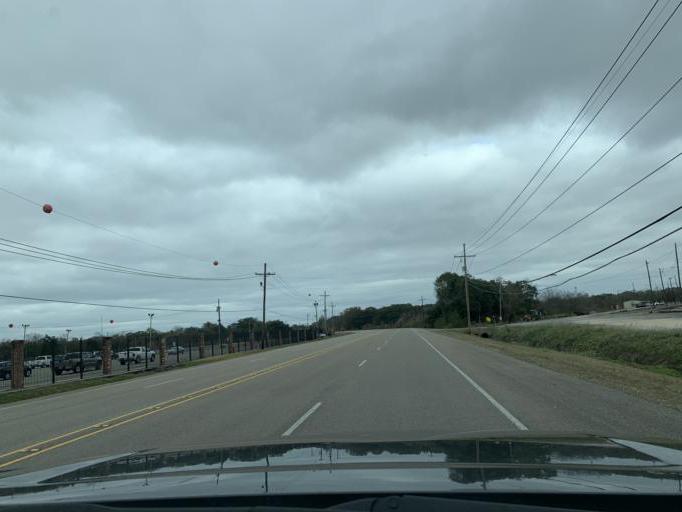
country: US
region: Louisiana
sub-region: Jefferson Parish
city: Avondale
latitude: 29.9191
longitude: -90.1857
